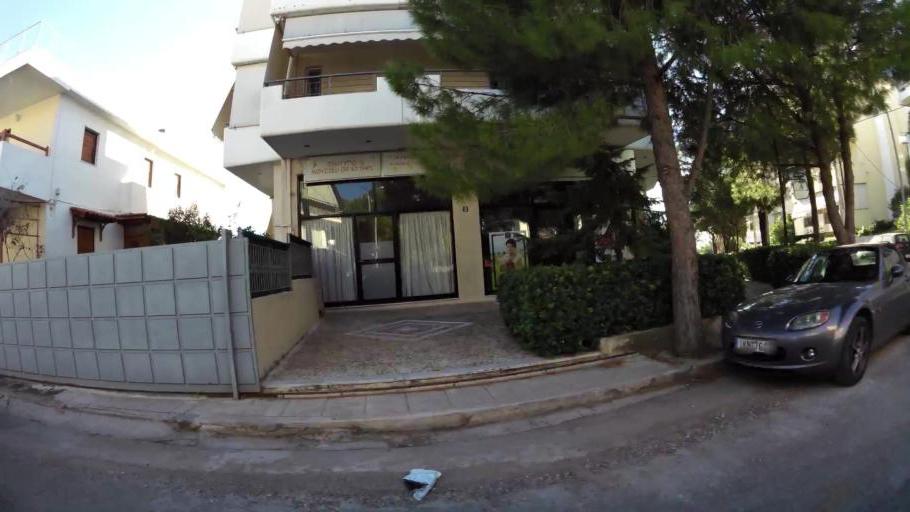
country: GR
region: Attica
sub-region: Nomarchia Athinas
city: Melissia
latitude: 38.0471
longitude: 23.8422
